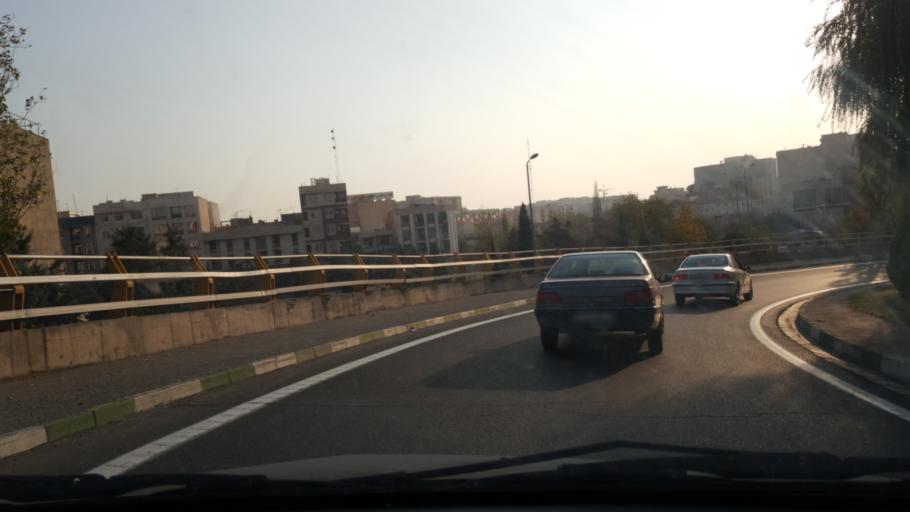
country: IR
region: Tehran
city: Tehran
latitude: 35.7325
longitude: 51.2964
